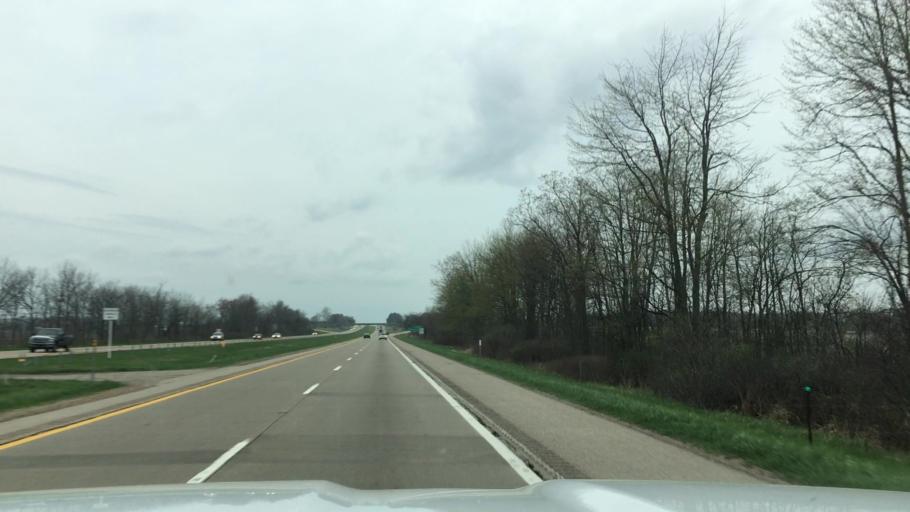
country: US
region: Michigan
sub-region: Ionia County
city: Saranac
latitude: 42.8796
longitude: -85.2300
